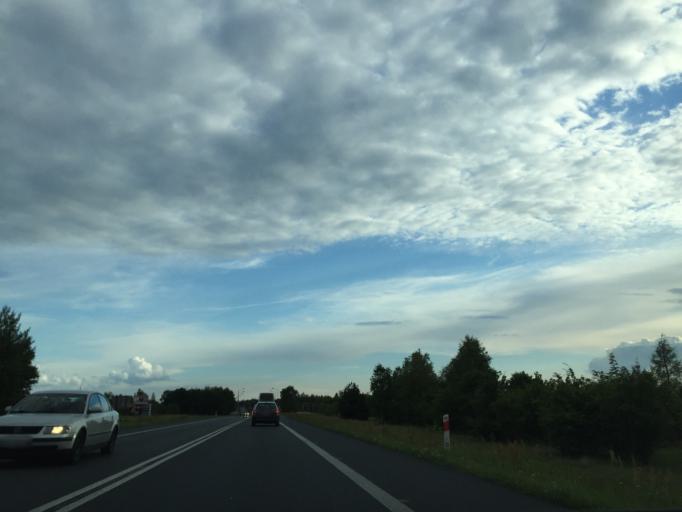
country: PL
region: Lublin Voivodeship
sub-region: Powiat lubartowski
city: Lubartow
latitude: 51.4676
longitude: 22.5802
